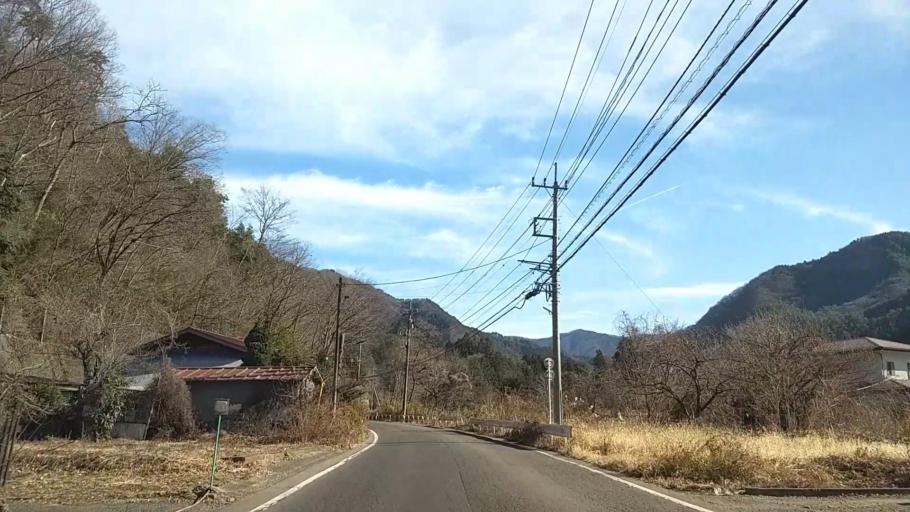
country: JP
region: Yamanashi
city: Otsuki
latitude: 35.5331
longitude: 138.9113
